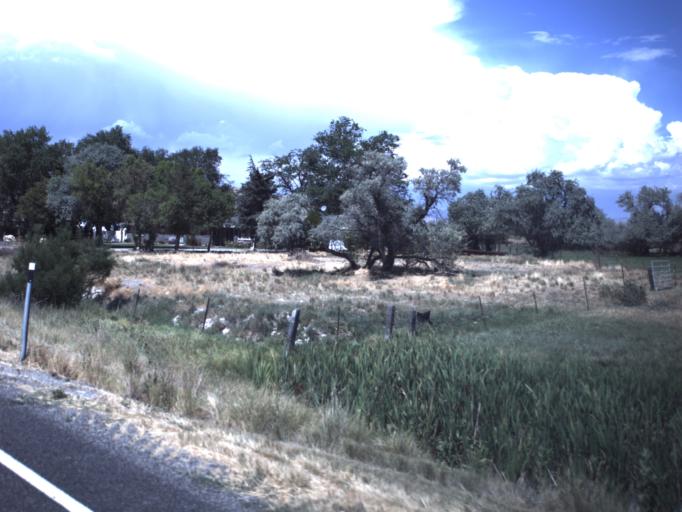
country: US
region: Utah
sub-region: Box Elder County
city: Honeyville
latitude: 41.5639
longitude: -112.1716
